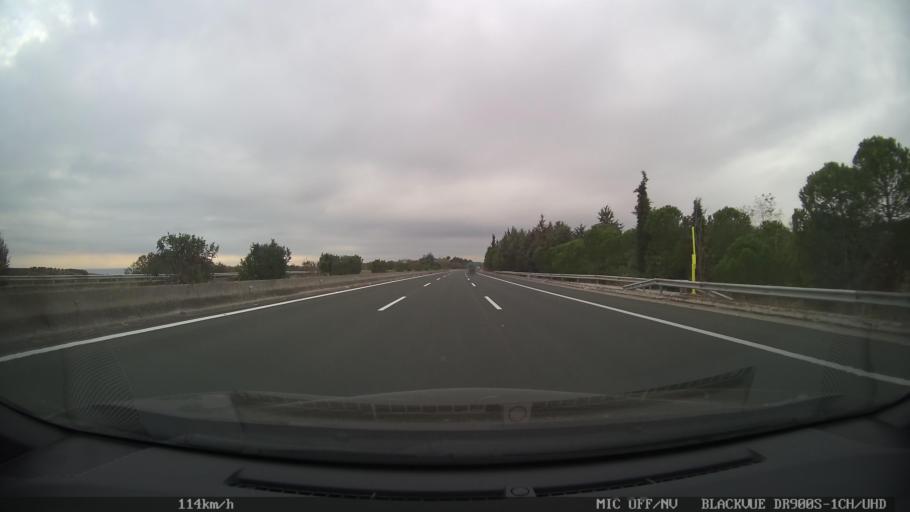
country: GR
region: Central Macedonia
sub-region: Nomos Pierias
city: Makrygialos
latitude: 40.4308
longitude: 22.5879
